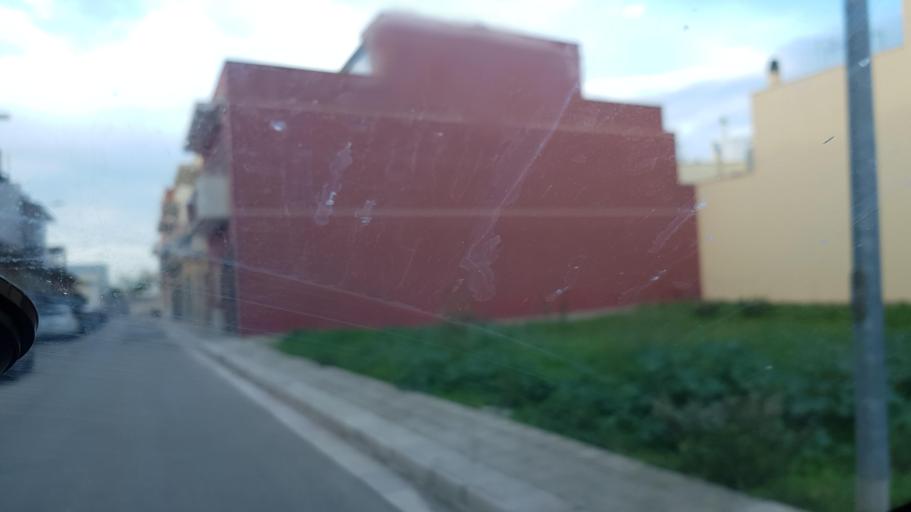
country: IT
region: Apulia
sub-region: Provincia di Brindisi
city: San Vito dei Normanni
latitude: 40.6602
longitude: 17.7082
